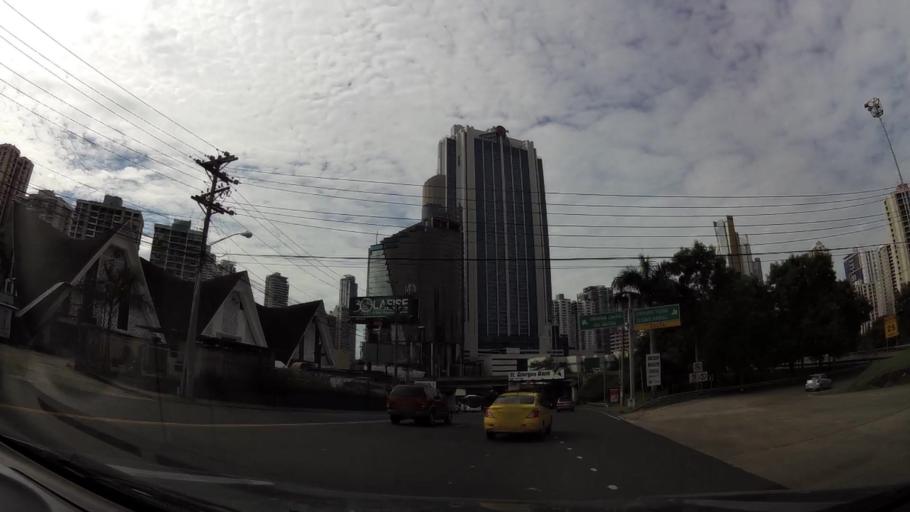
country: PA
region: Panama
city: Panama
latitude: 8.9800
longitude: -79.5162
